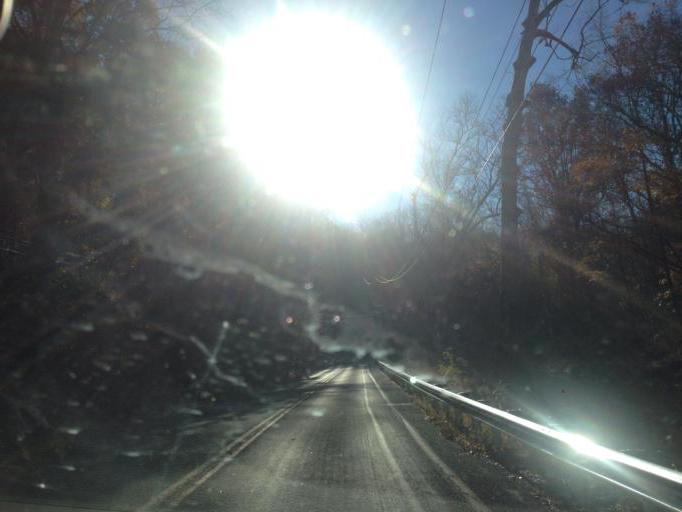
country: US
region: Maryland
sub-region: Howard County
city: Riverside
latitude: 39.1876
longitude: -76.8913
